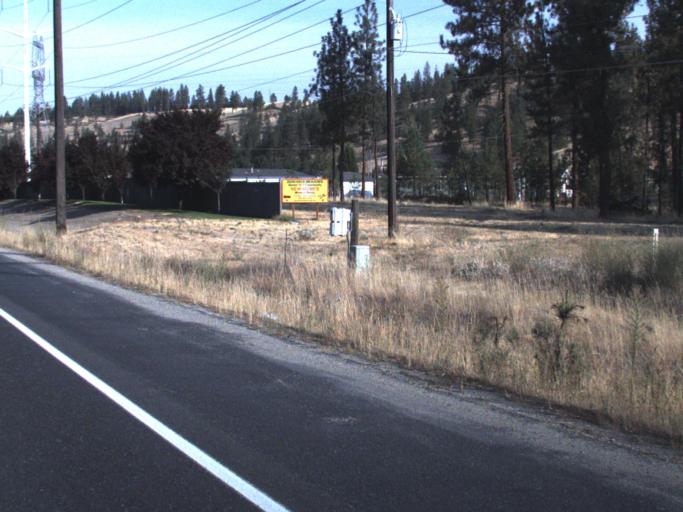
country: US
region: Washington
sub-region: Spokane County
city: Town and Country
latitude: 47.7509
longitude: -117.5108
